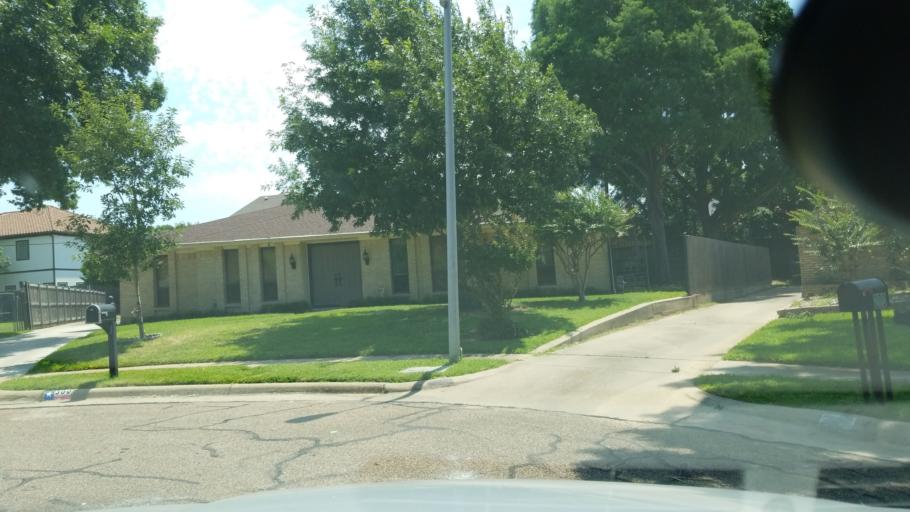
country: US
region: Texas
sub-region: Dallas County
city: Irving
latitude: 32.8489
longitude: -96.9445
